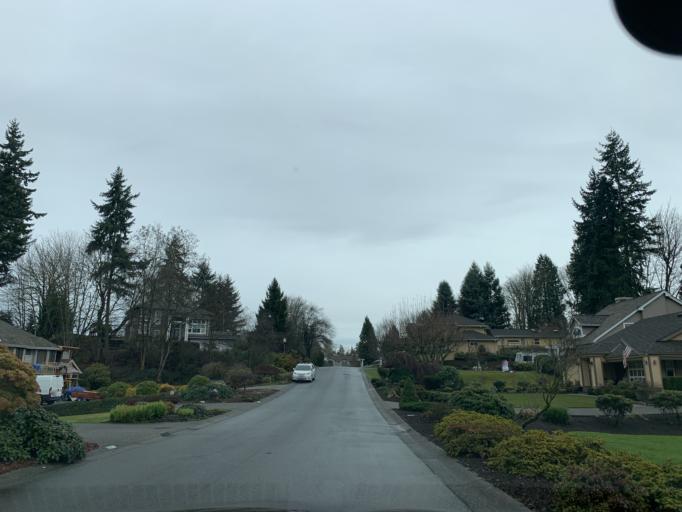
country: US
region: Washington
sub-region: King County
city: Bothell
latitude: 47.7443
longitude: -122.1938
